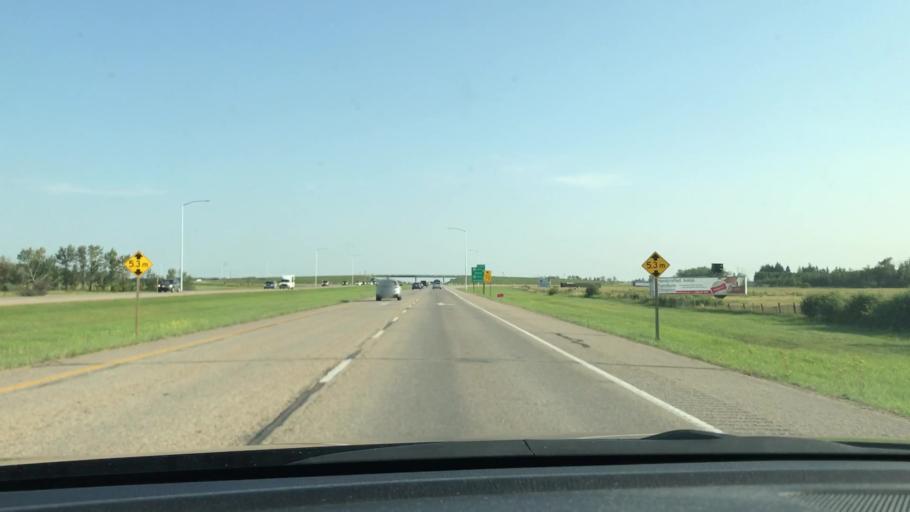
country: CA
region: Alberta
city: Millet
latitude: 53.0971
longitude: -113.5983
